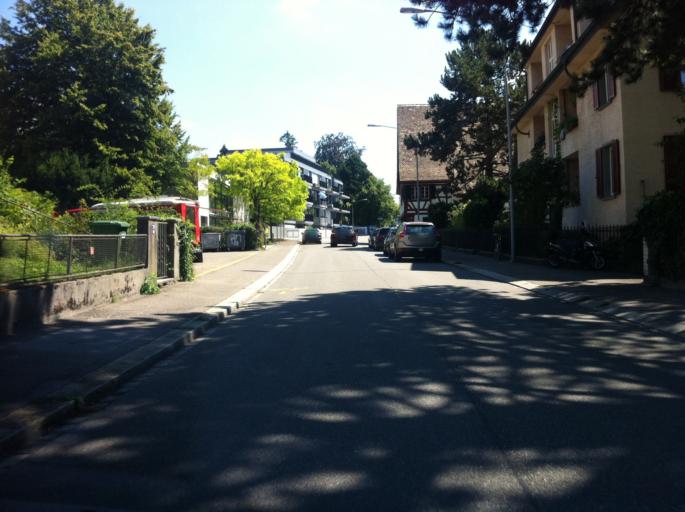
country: CH
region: Zurich
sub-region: Bezirk Zuerich
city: Zuerich (Kreis 8)
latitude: 47.3509
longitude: 8.5635
